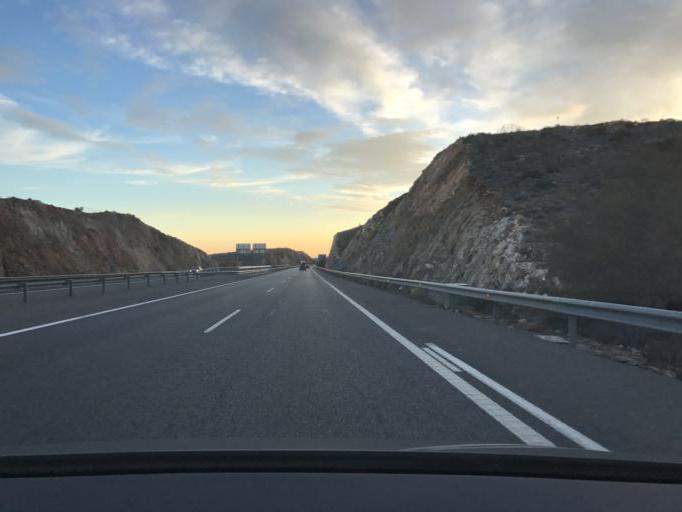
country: ES
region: Andalusia
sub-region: Provincia de Almeria
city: Huercal de Almeria
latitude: 36.8690
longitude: -2.4628
